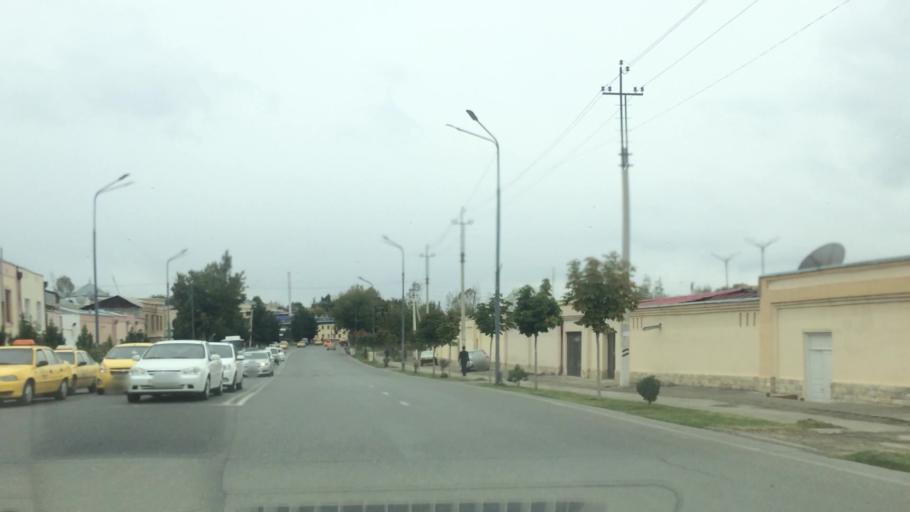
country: UZ
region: Samarqand
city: Samarqand
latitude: 39.6575
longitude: 66.9709
